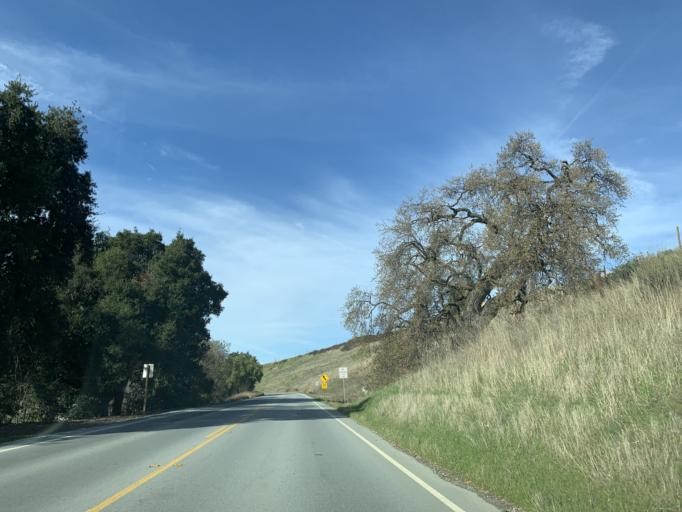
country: US
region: California
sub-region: San Benito County
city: Ridgemark
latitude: 36.7700
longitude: -121.3044
